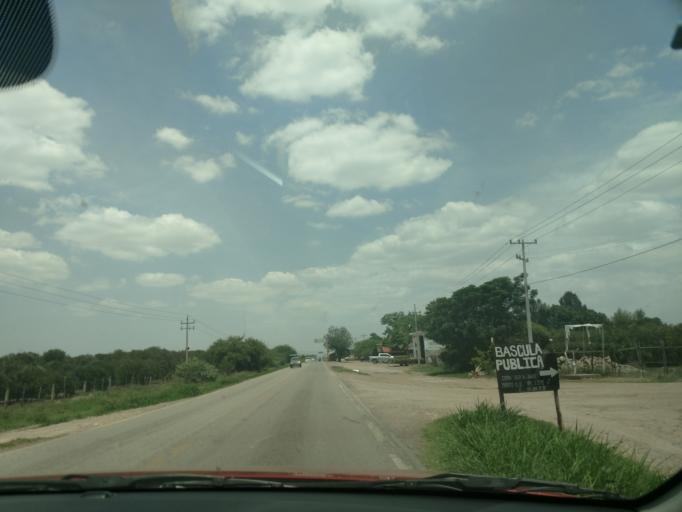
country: MX
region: San Luis Potosi
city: Ciudad Fernandez
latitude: 21.9481
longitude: -100.0576
